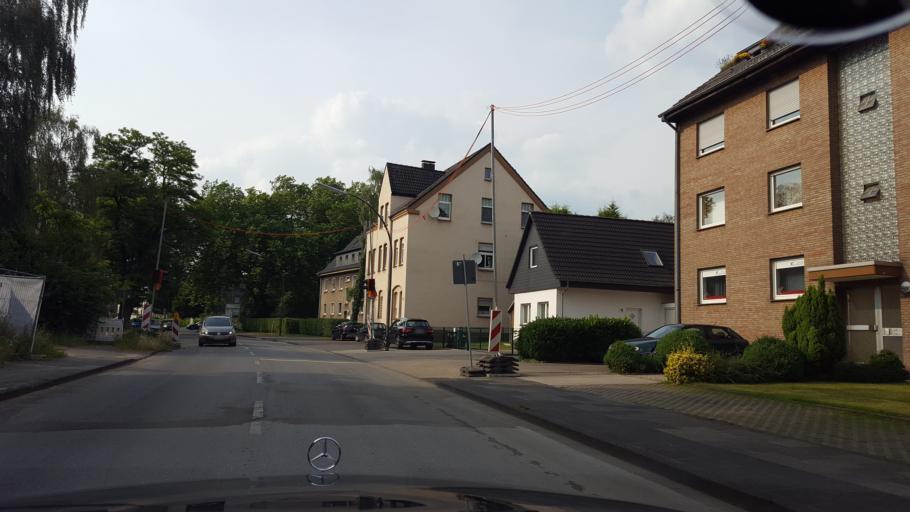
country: DE
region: North Rhine-Westphalia
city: Oer-Erkenschwick
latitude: 51.6087
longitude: 7.2720
